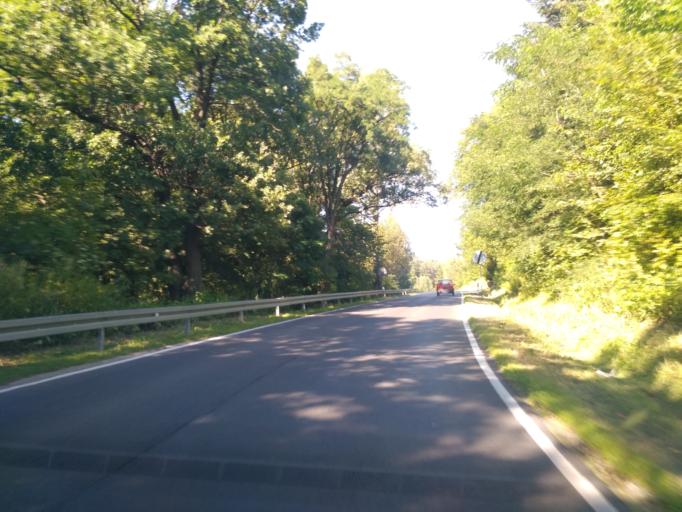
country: PL
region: Subcarpathian Voivodeship
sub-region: Powiat krosnienski
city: Korczyna
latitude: 49.7365
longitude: 21.8060
